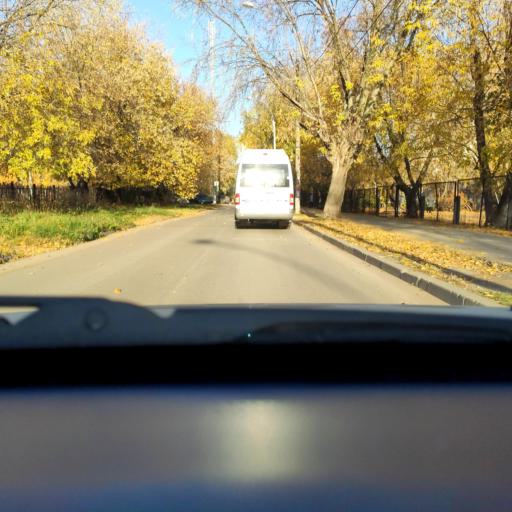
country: RU
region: Perm
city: Perm
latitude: 57.9758
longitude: 56.2359
